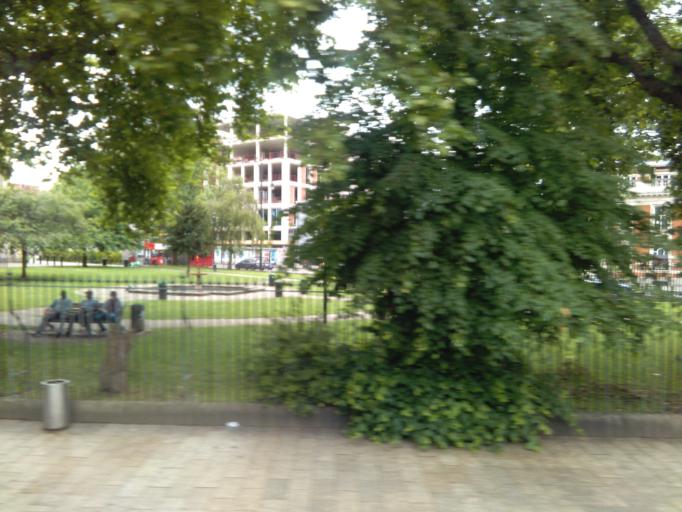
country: GB
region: England
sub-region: Greater London
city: Brixton Hill
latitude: 51.4603
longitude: -0.1159
